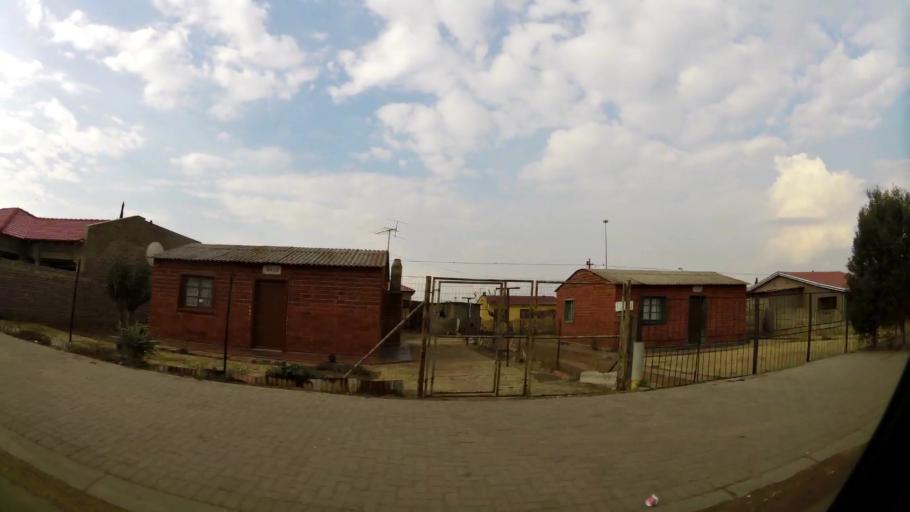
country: ZA
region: Gauteng
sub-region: Sedibeng District Municipality
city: Vanderbijlpark
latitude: -26.6858
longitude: 27.8686
